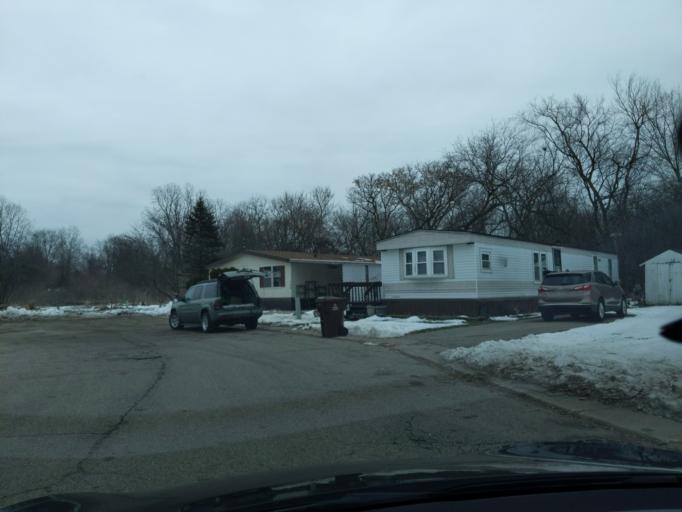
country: US
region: Michigan
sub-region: Ingham County
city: Lansing
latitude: 42.7724
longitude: -84.5507
